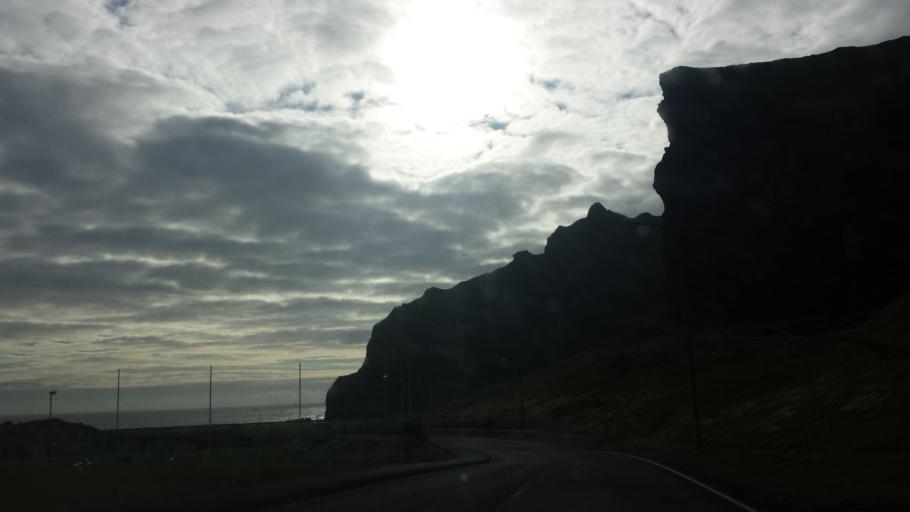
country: IS
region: South
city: Vestmannaeyjar
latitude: 63.4399
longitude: -20.2851
